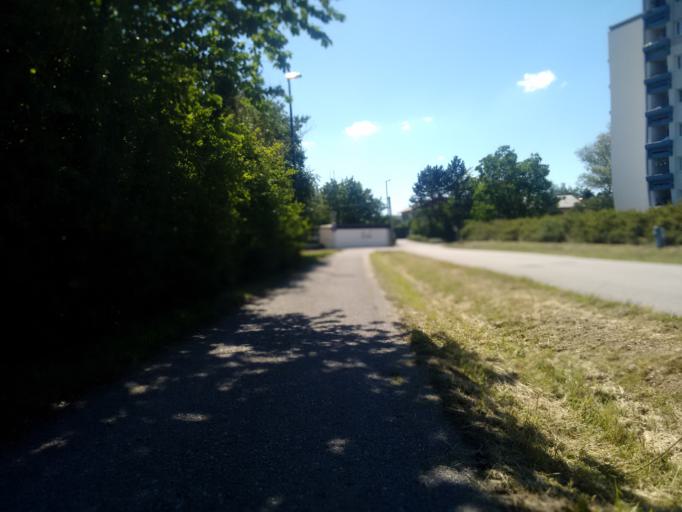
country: AT
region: Upper Austria
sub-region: Wels-Land
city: Steinhaus
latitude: 48.1433
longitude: 13.9961
